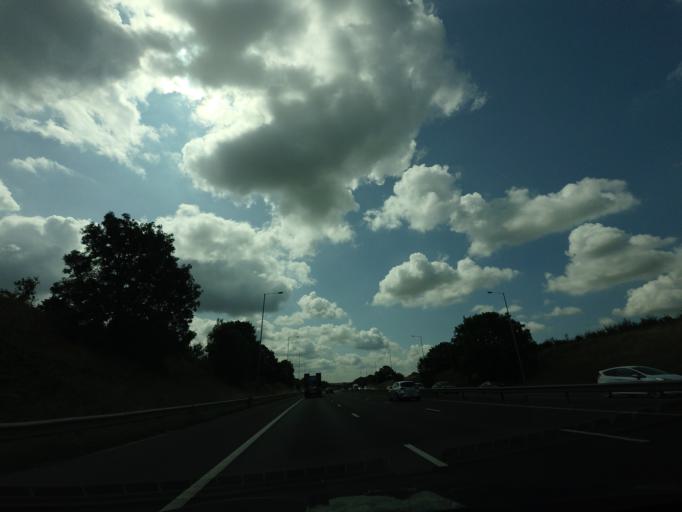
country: GB
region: England
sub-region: Lancashire
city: Euxton
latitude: 53.6725
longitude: -2.6856
